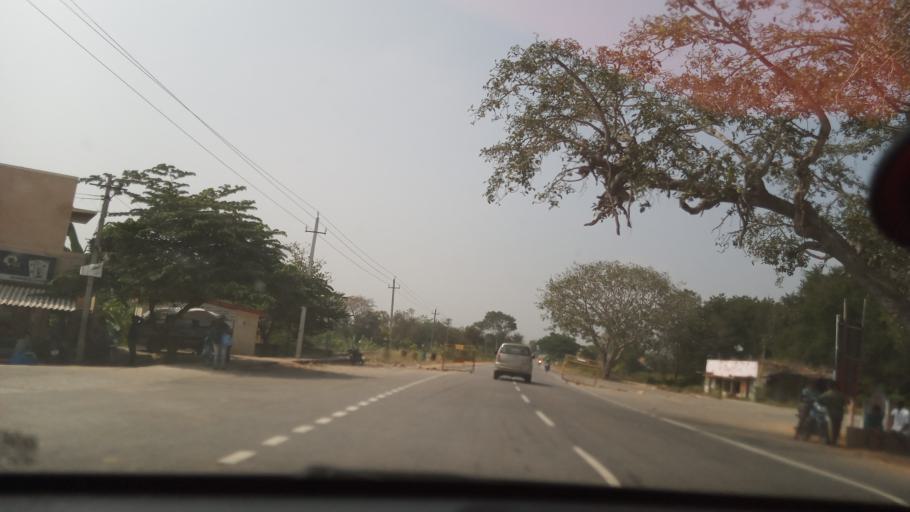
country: IN
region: Karnataka
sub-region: Mysore
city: Nanjangud
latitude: 12.0679
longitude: 76.7492
